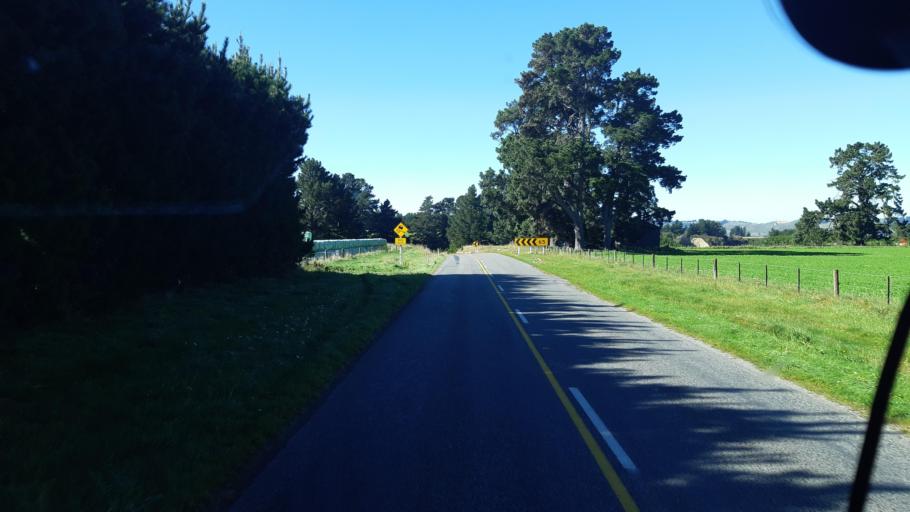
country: NZ
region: Canterbury
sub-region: Waimakariri District
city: Oxford
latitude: -43.2268
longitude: 172.3012
